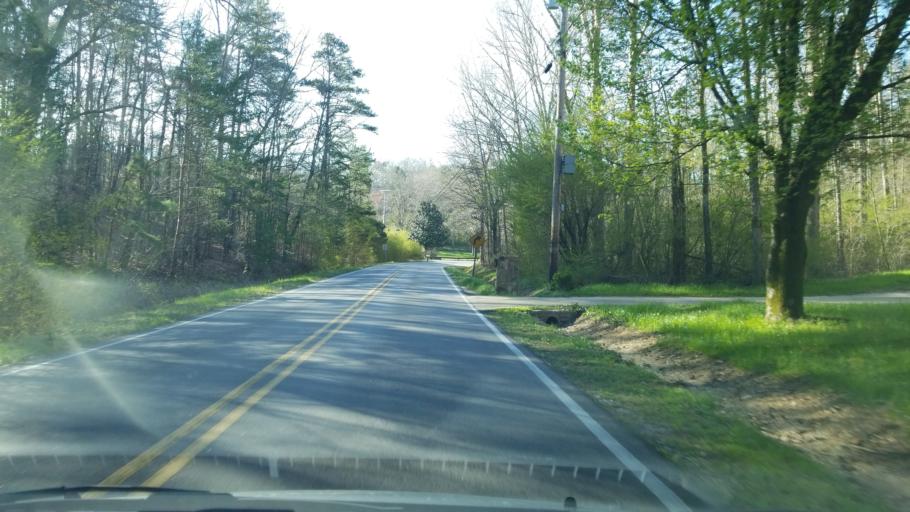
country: US
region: Tennessee
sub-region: Hamilton County
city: East Brainerd
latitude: 35.0165
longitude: -85.1126
